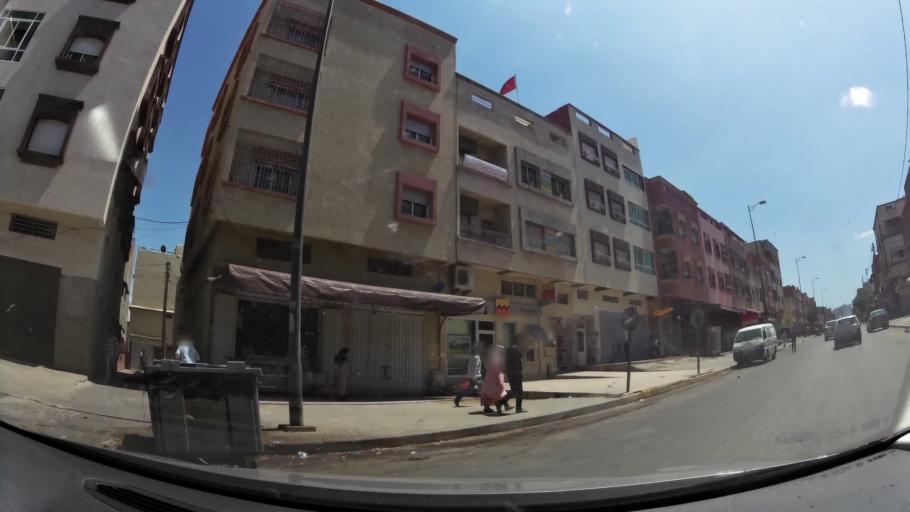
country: MA
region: Gharb-Chrarda-Beni Hssen
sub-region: Kenitra Province
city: Kenitra
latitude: 34.2475
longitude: -6.5446
